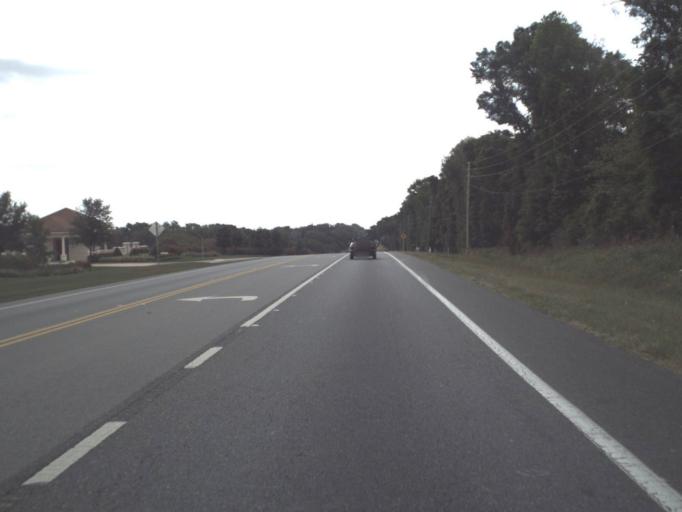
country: US
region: Florida
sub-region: Marion County
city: Ocala
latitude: 29.2595
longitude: -82.1427
